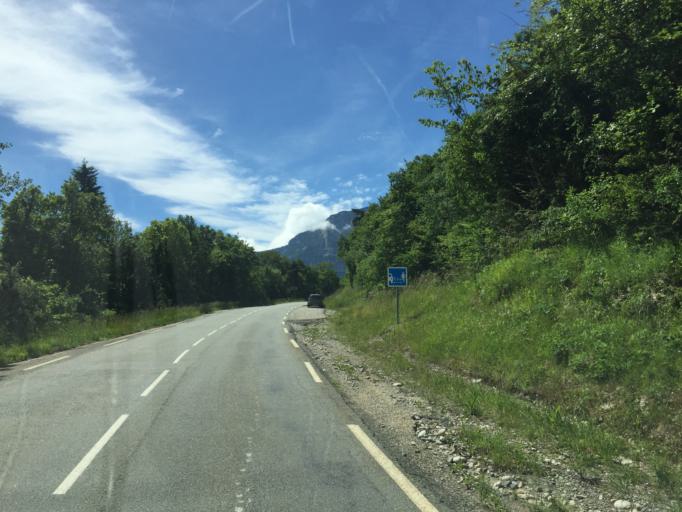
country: FR
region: Rhone-Alpes
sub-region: Departement de la Savoie
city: Saint-Baldoph
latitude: 45.5125
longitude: 5.9261
